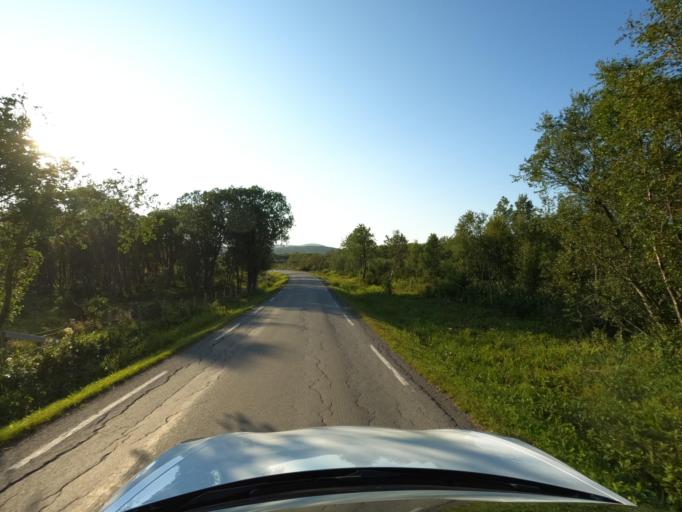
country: NO
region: Troms
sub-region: Skanland
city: Evenskjer
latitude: 68.4627
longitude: 16.6755
